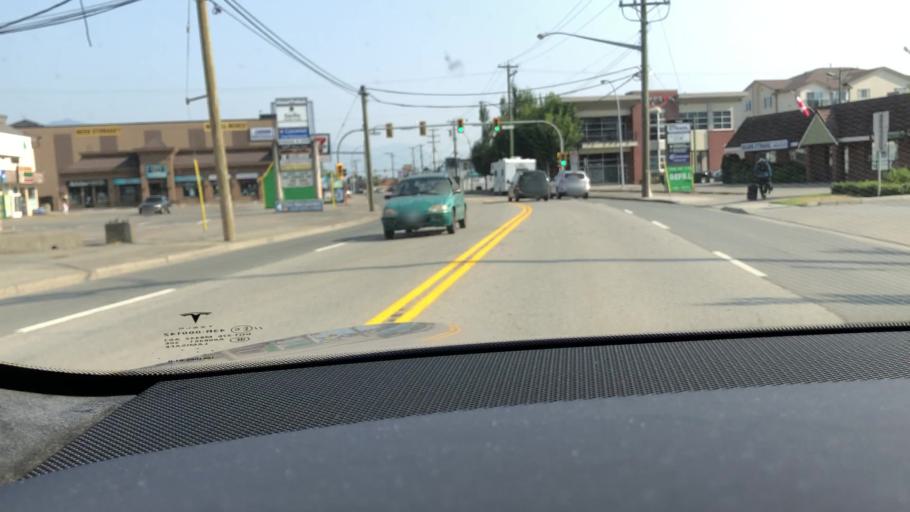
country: CA
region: British Columbia
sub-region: Fraser Valley Regional District
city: Chilliwack
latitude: 49.1356
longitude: -121.9592
